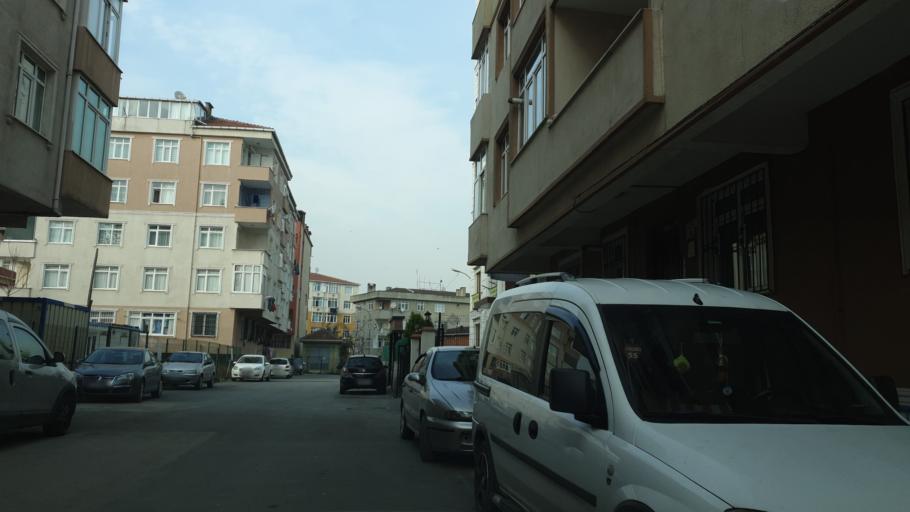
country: TR
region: Istanbul
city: Pendik
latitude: 40.8774
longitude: 29.2753
